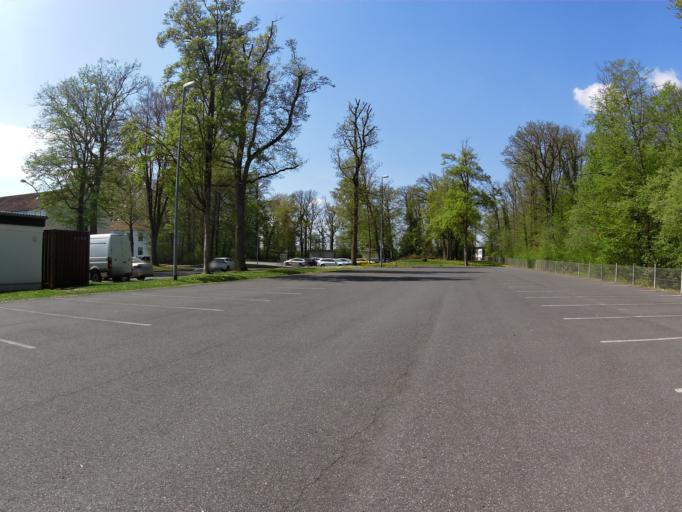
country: DE
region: Bavaria
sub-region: Regierungsbezirk Unterfranken
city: Giebelstadt
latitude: 49.6897
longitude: 9.9498
